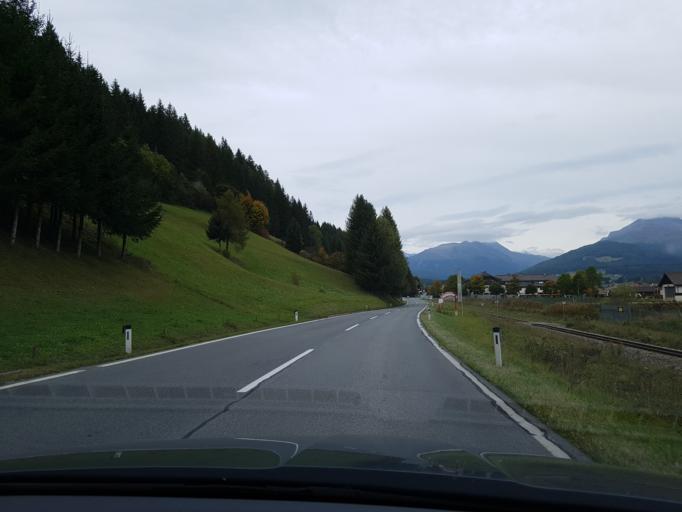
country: AT
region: Salzburg
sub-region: Politischer Bezirk Tamsweg
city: Tamsweg
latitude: 47.1193
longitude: 13.8106
